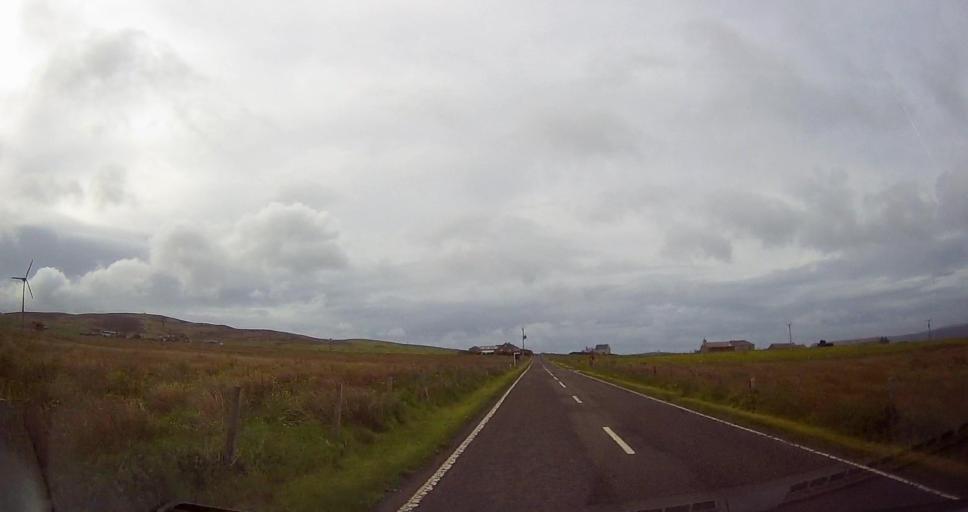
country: GB
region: Scotland
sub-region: Orkney Islands
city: Stromness
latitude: 58.9350
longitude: -3.2108
